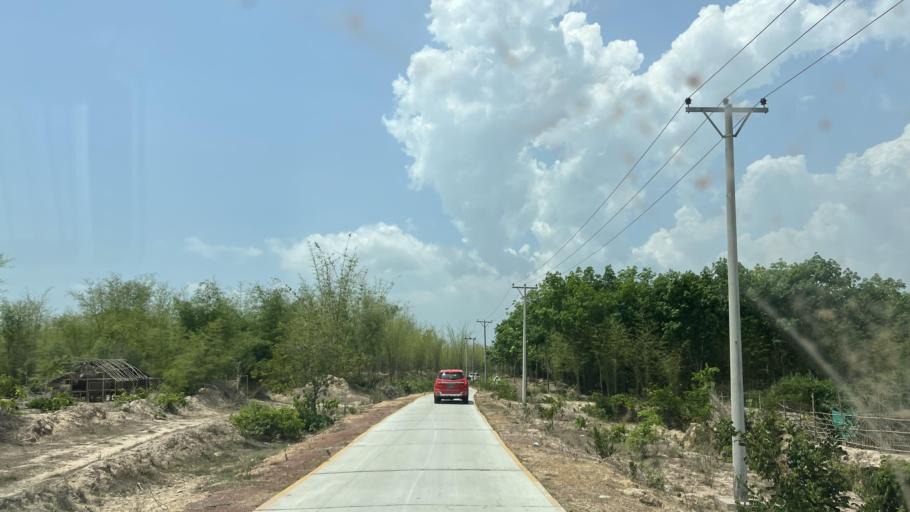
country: MM
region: Yangon
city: Twante
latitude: 16.5969
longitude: 95.9426
